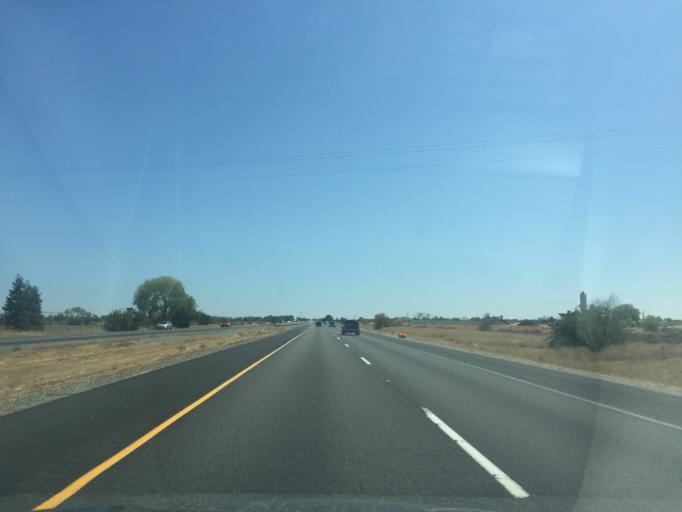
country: US
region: California
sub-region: Tehama County
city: Corning
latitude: 39.9821
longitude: -122.2030
